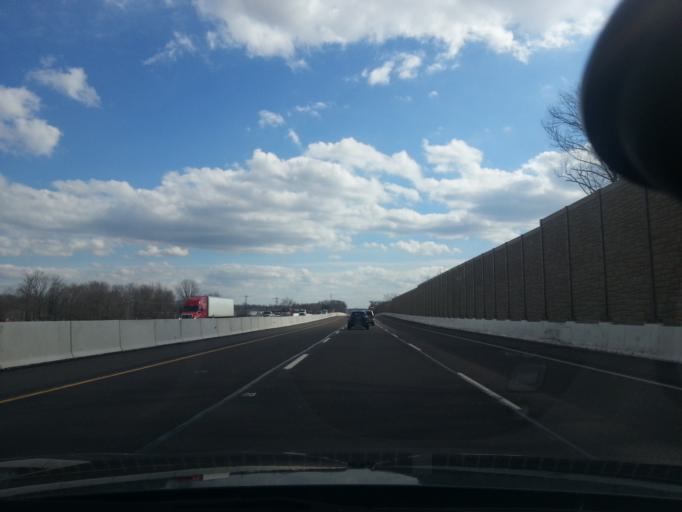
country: US
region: Pennsylvania
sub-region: Montgomery County
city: Blue Bell
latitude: 40.1396
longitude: -75.2890
